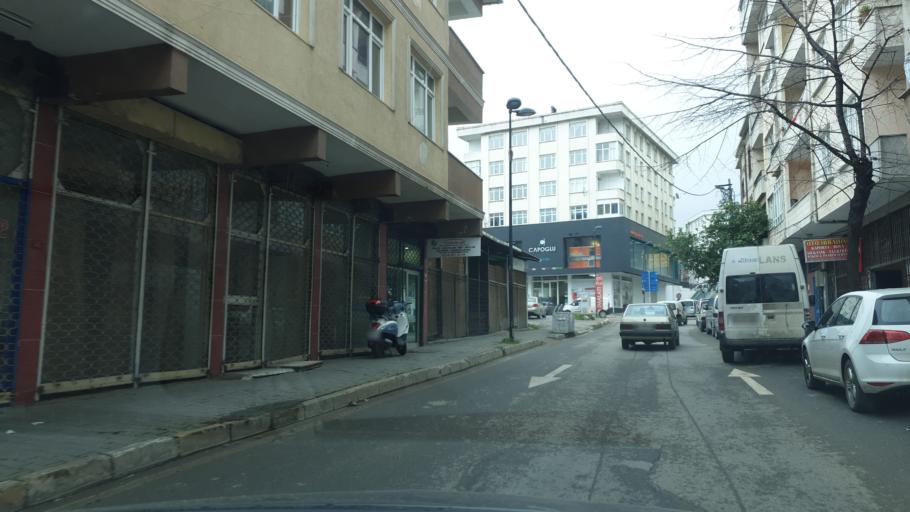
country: TR
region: Istanbul
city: Pendik
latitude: 40.8716
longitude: 29.2654
